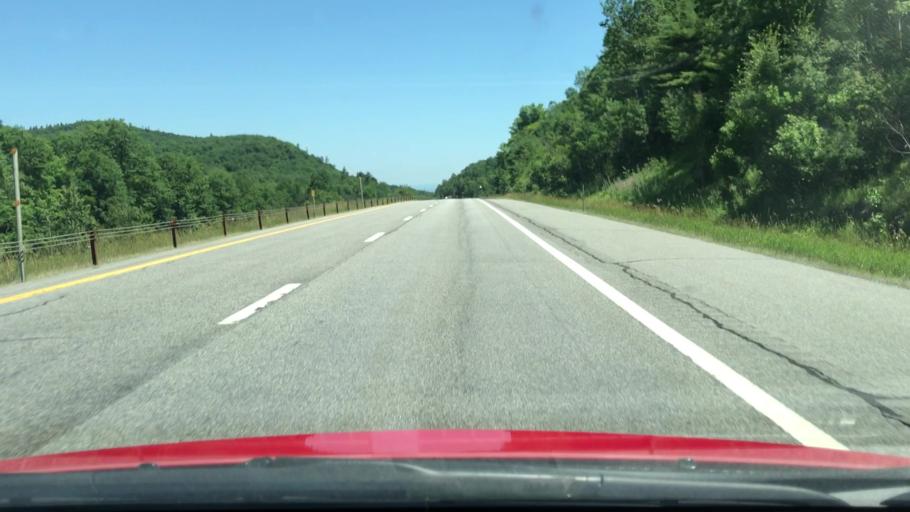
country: US
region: New York
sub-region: Essex County
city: Elizabethtown
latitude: 44.1803
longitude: -73.5749
